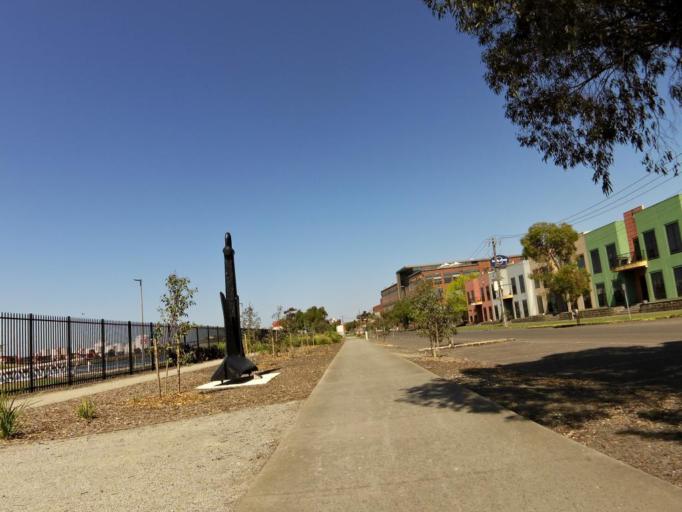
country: AU
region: Victoria
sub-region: Maribyrnong
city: Footscray
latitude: -37.8069
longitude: 144.9066
